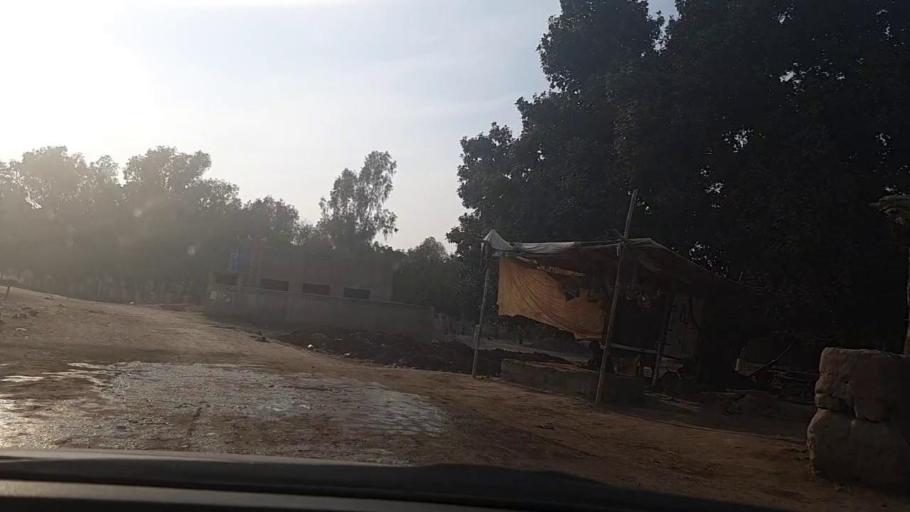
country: PK
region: Sindh
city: Daulatpur
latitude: 26.3342
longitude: 68.0482
